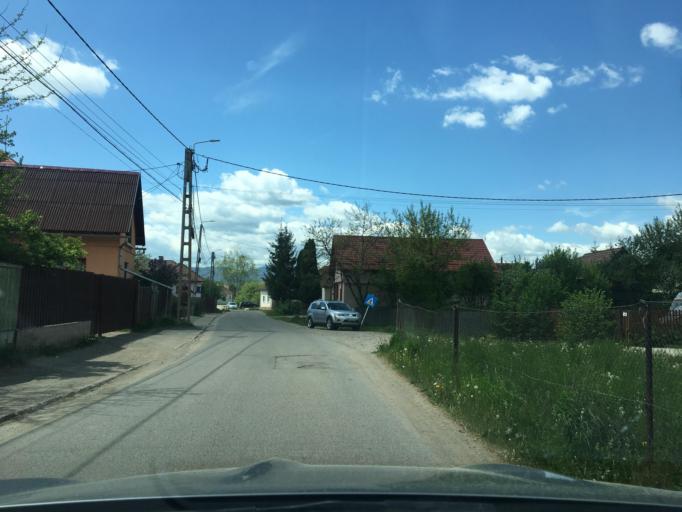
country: RO
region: Harghita
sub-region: Comuna Ditrau
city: Ditrau
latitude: 46.7995
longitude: 25.4888
